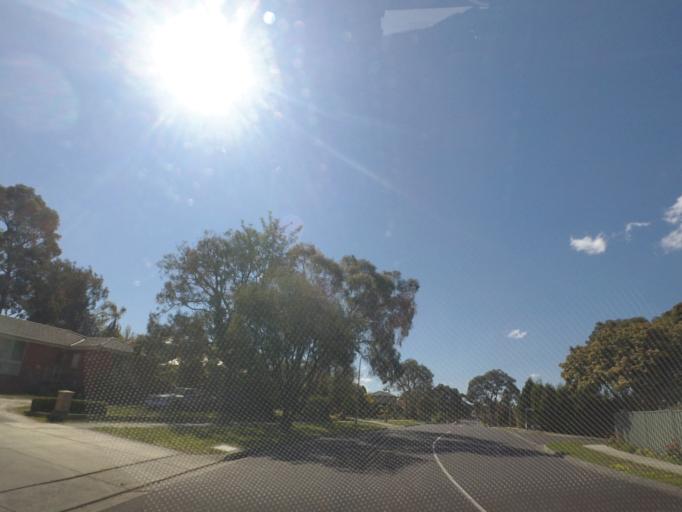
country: AU
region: Victoria
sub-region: Knox
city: Wantirna
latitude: -37.8647
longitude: 145.2249
